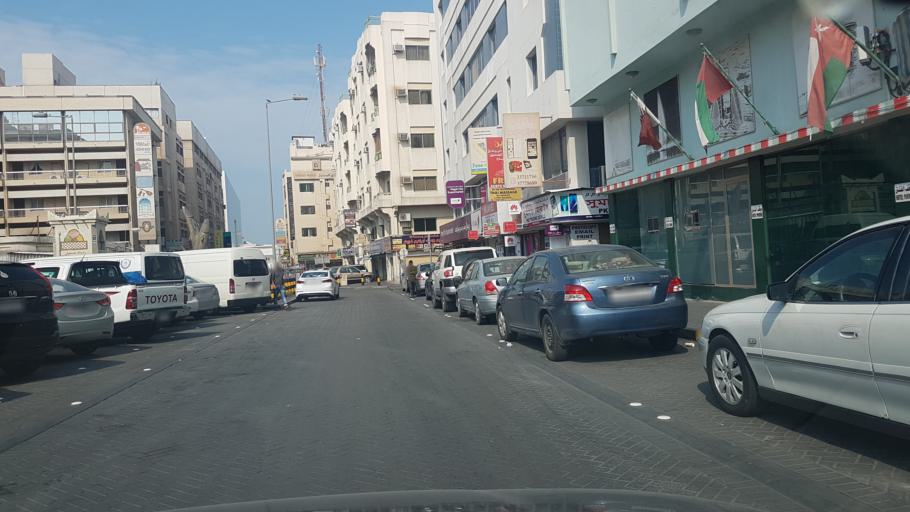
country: BH
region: Manama
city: Manama
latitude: 26.2308
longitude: 50.5743
